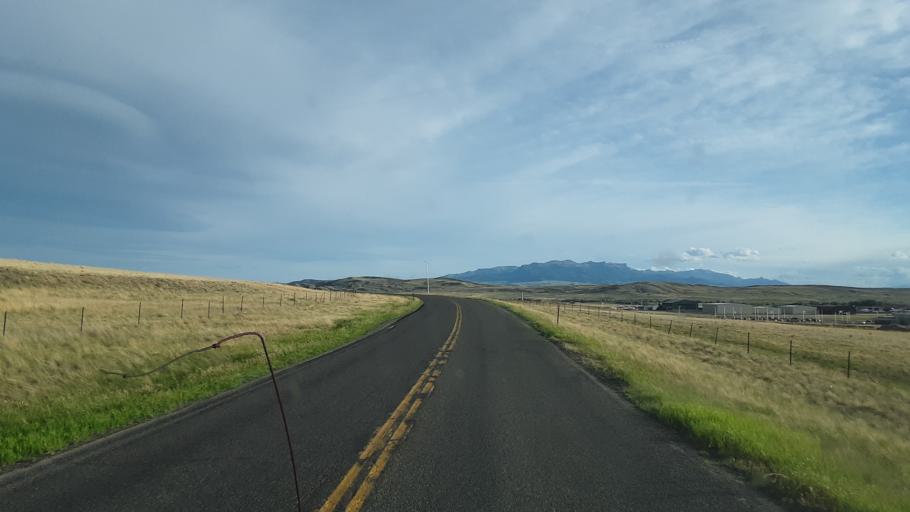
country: US
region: Wyoming
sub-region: Park County
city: Cody
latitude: 44.5207
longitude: -109.0165
